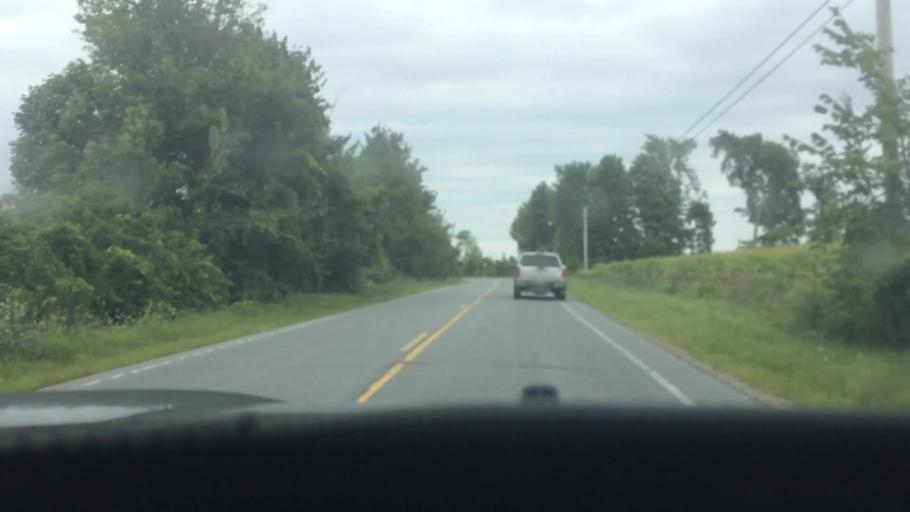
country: US
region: New York
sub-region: St. Lawrence County
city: Canton
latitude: 44.4895
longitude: -75.2174
